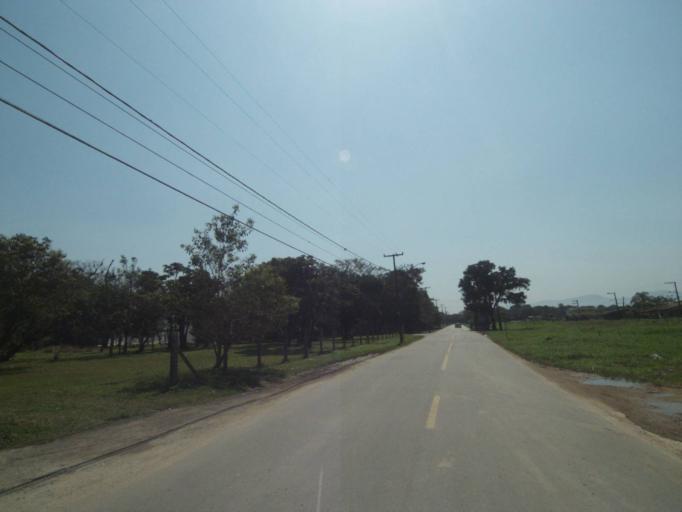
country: BR
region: Parana
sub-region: Paranagua
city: Paranagua
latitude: -25.5537
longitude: -48.6273
